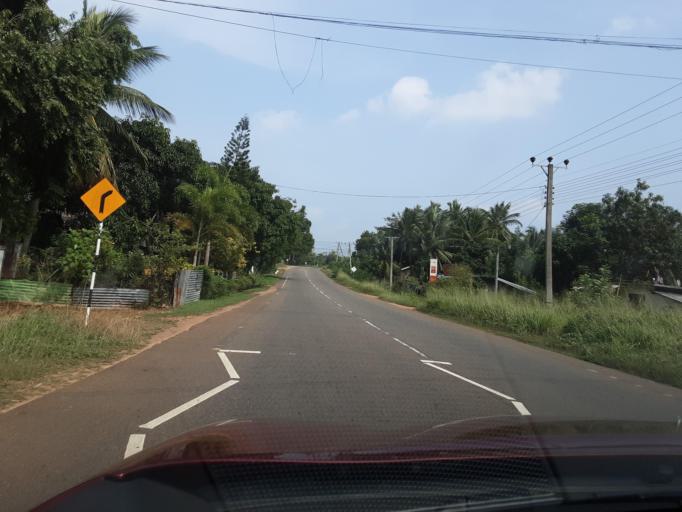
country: LK
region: North Central
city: Anuradhapura
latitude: 8.3374
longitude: 80.5020
